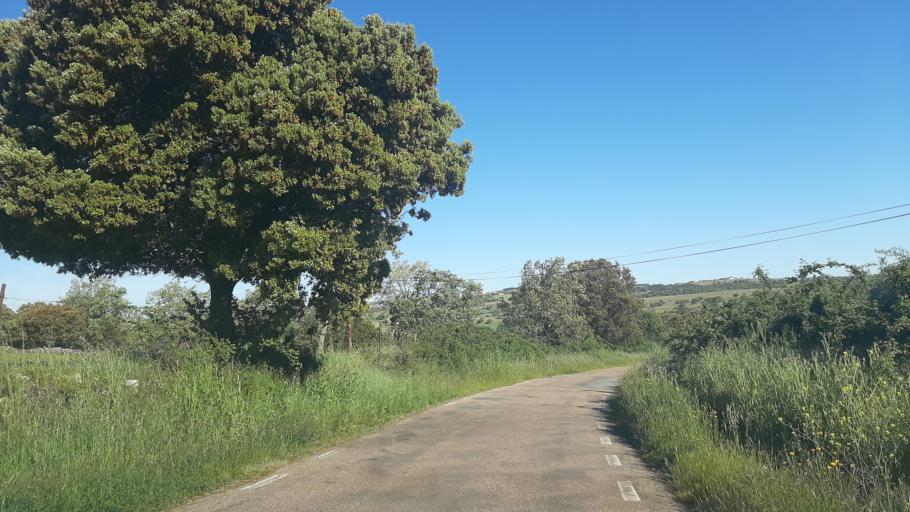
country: ES
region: Castille and Leon
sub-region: Provincia de Salamanca
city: Guijo de Avila
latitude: 40.5306
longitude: -5.6439
